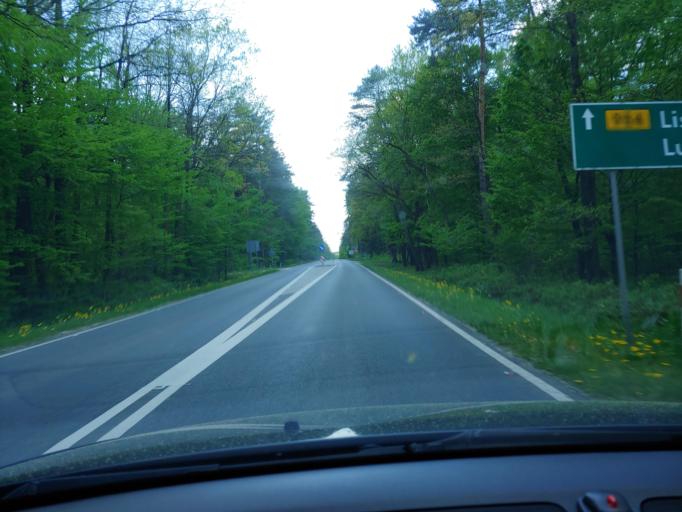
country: PL
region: Lesser Poland Voivodeship
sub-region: Powiat dabrowski
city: Radgoszcz
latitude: 50.1367
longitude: 21.1655
